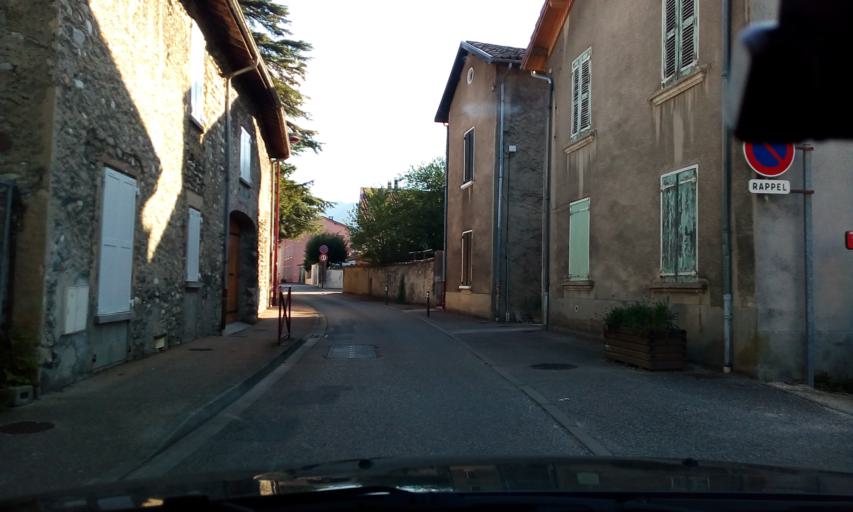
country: FR
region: Rhone-Alpes
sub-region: Departement de l'Isere
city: Vif
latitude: 45.0583
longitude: 5.6713
